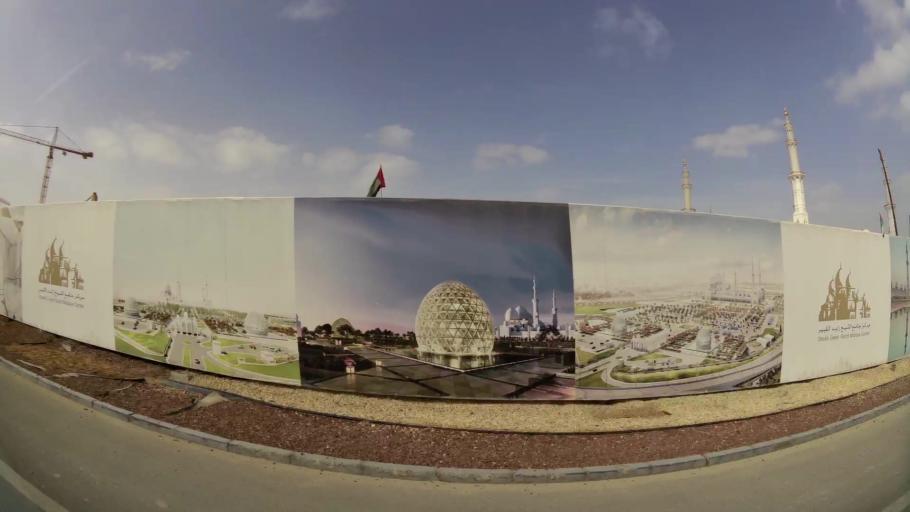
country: AE
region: Abu Dhabi
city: Abu Dhabi
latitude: 24.4102
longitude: 54.4780
